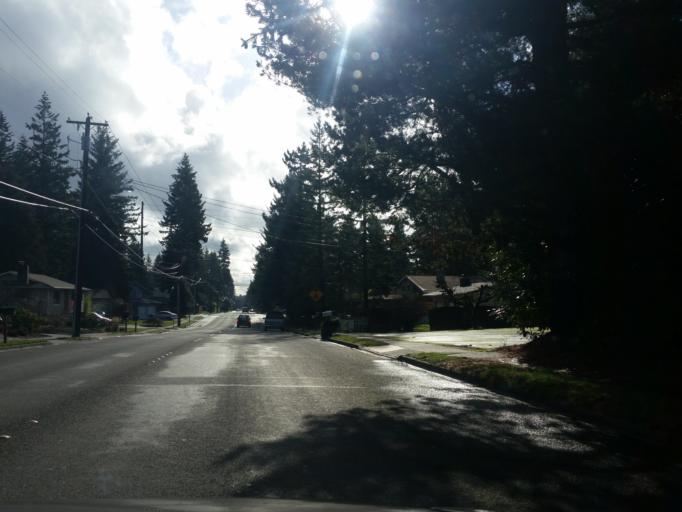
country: US
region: Washington
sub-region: Snohomish County
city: Lynnwood
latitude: 47.8300
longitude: -122.3197
